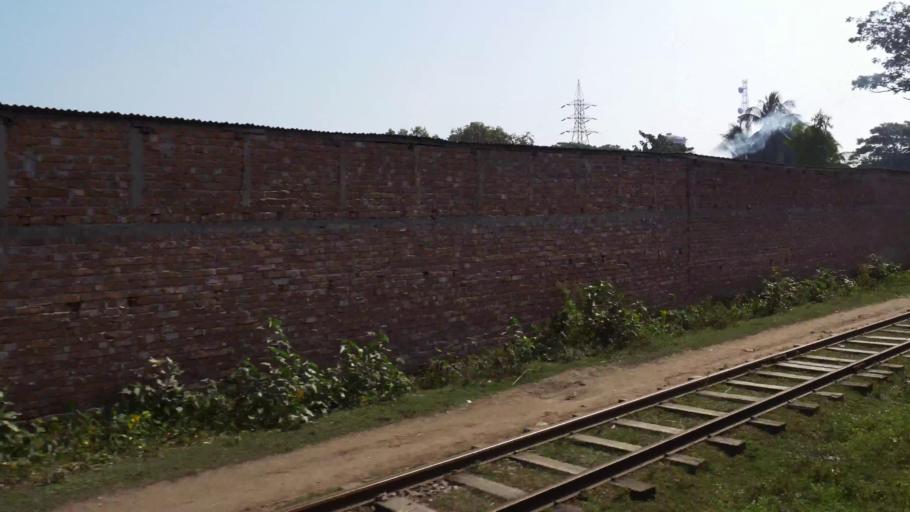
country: BD
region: Dhaka
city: Mymensingh
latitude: 24.6131
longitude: 90.4817
